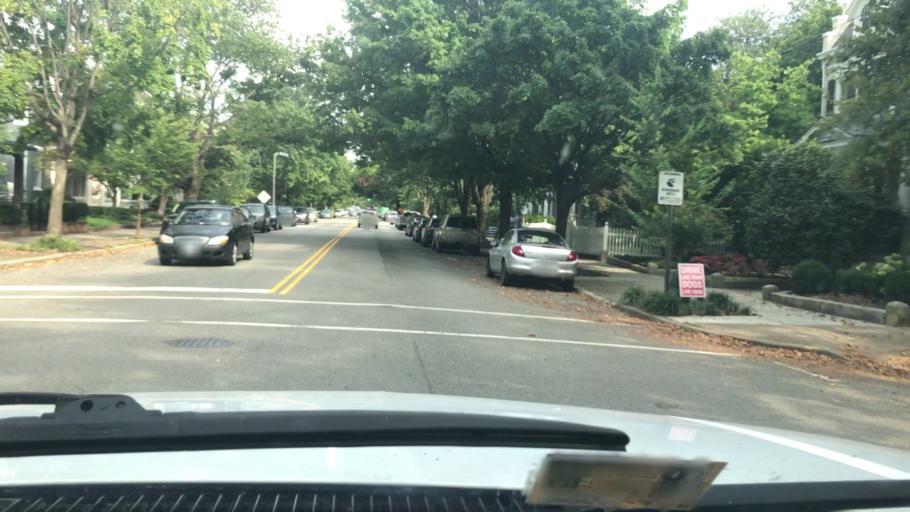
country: US
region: Virginia
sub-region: City of Richmond
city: Richmond
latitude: 37.5528
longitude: -77.4683
